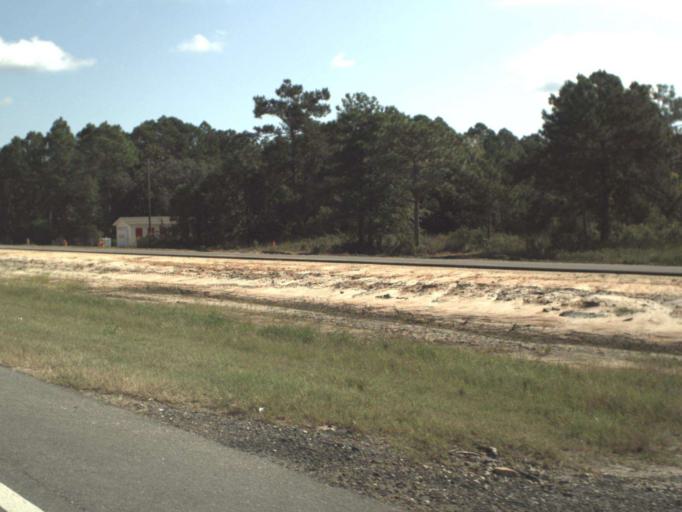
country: US
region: Florida
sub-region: Walton County
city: Freeport
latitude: 30.4378
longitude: -86.1502
